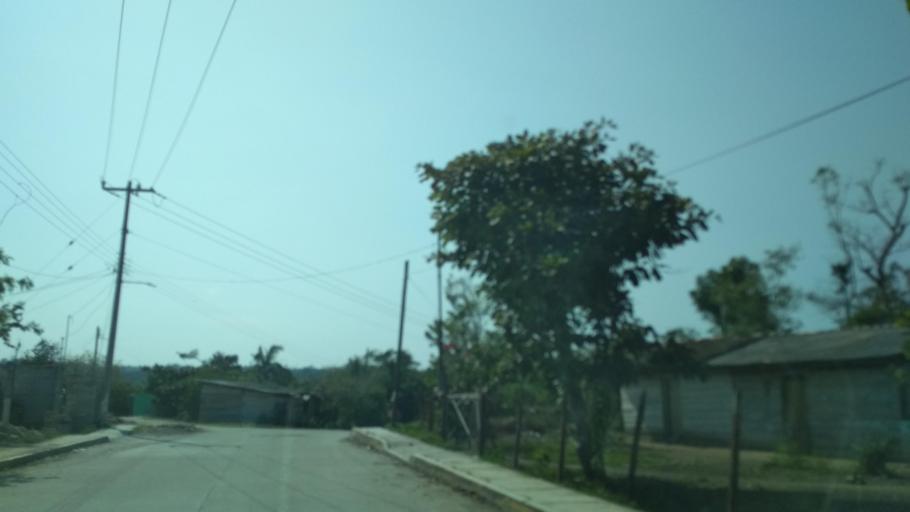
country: MX
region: Veracruz
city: Agua Dulce
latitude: 20.3951
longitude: -97.2088
